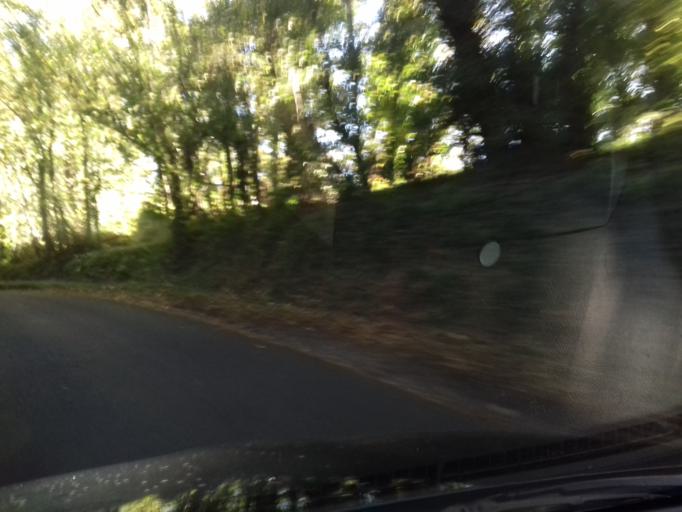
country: IE
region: Leinster
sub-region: Lu
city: Tullyallen
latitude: 53.7169
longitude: -6.3908
